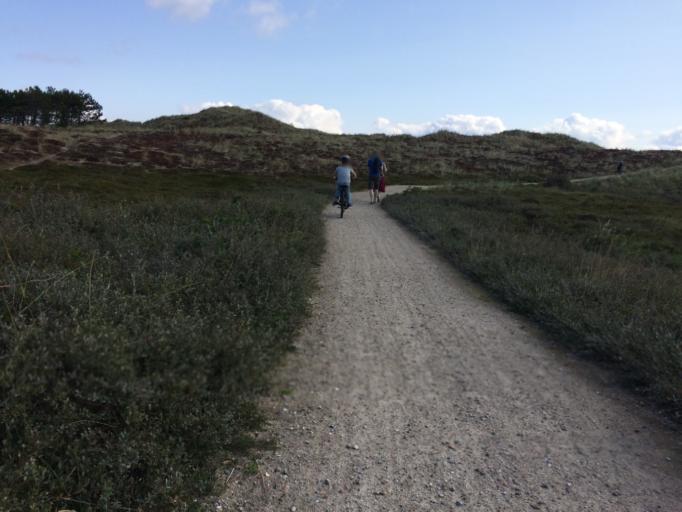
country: DK
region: Central Jutland
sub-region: Ringkobing-Skjern Kommune
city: Hvide Sande
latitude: 55.9450
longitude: 8.1505
